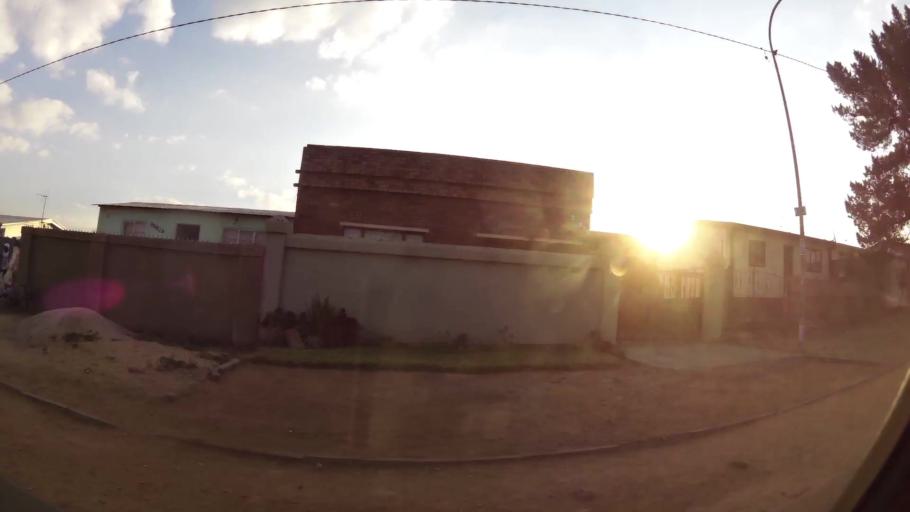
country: ZA
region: Gauteng
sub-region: City of Johannesburg Metropolitan Municipality
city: Soweto
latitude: -26.2239
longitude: 27.9089
